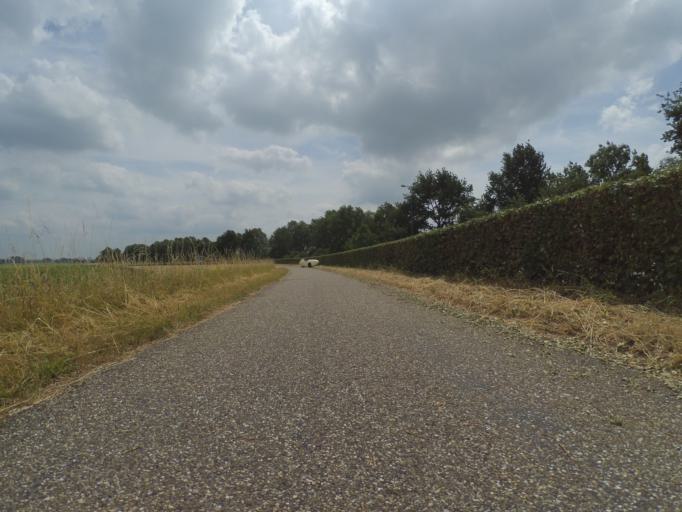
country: NL
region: Gelderland
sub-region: Gemeente Culemborg
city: Culemborg
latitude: 51.9858
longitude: 5.2468
